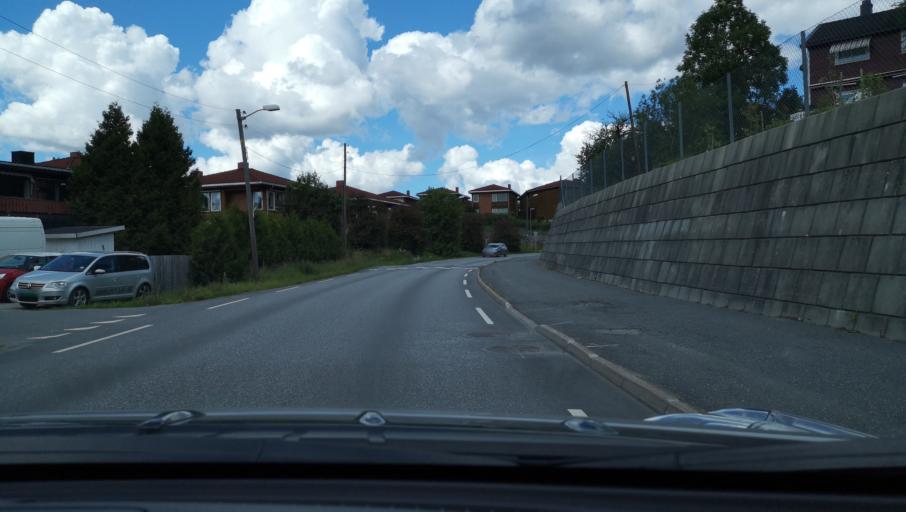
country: NO
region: Ostfold
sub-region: Hobol
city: Tomter
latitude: 59.6618
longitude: 10.9963
